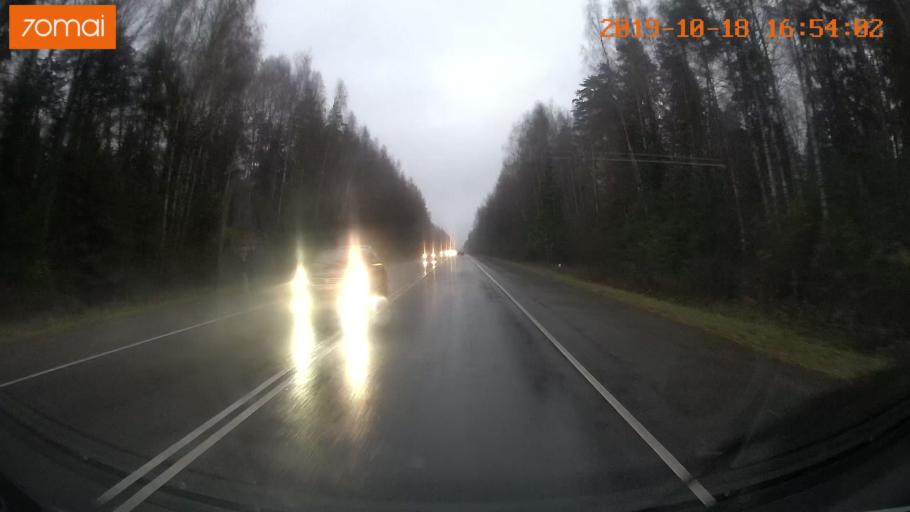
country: RU
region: Ivanovo
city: Nerl'
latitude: 56.6237
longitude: 40.5660
